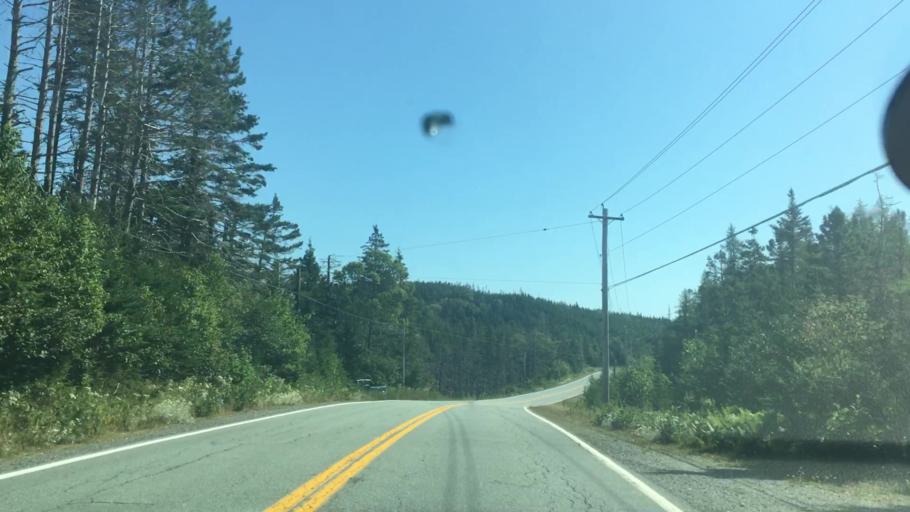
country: CA
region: Nova Scotia
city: Antigonish
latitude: 45.0125
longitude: -62.0949
